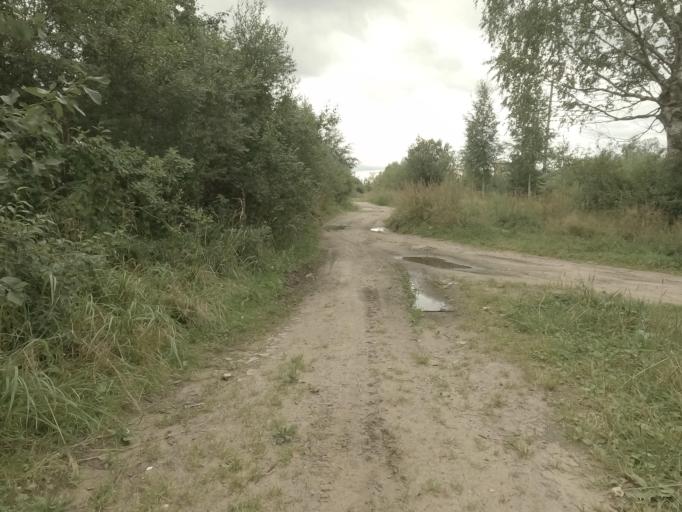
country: RU
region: Leningrad
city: Kirovsk
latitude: 59.8834
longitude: 31.0025
